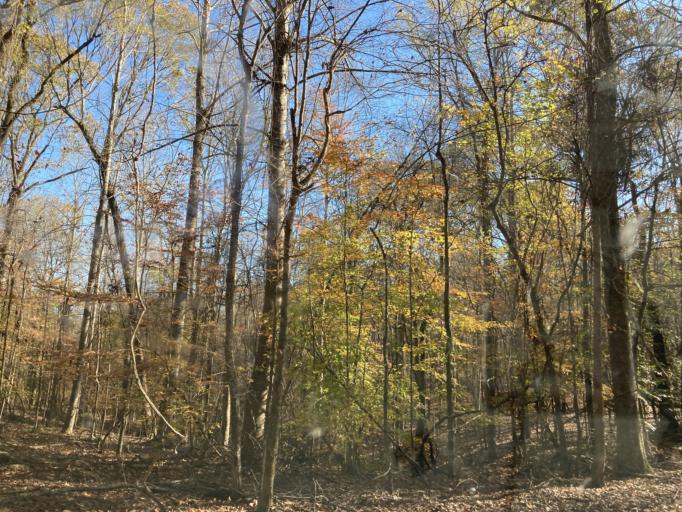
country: US
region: Mississippi
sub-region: Yazoo County
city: Yazoo City
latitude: 32.6726
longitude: -90.5065
